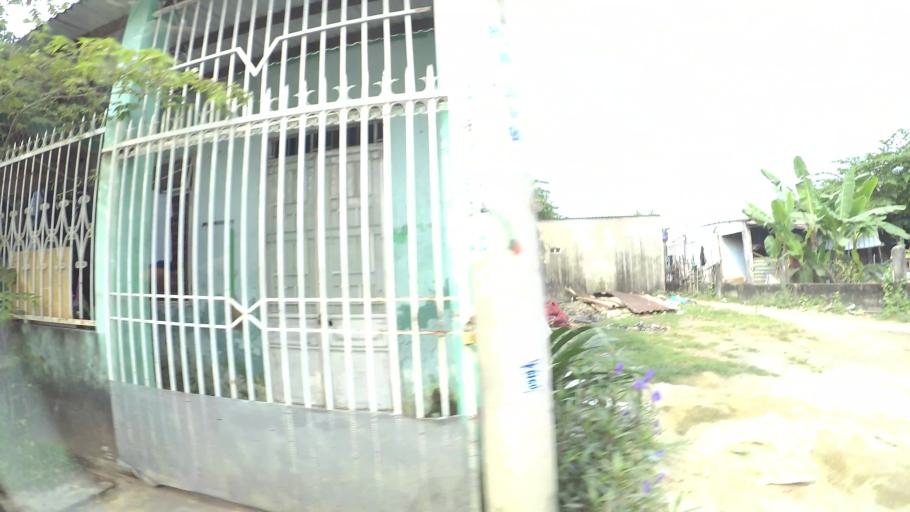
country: VN
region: Da Nang
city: Lien Chieu
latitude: 16.0587
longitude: 108.1583
